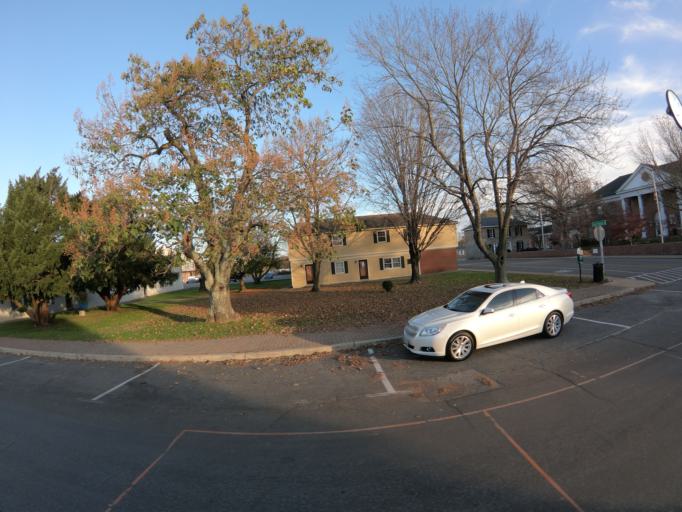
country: US
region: Maryland
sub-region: Saint Mary's County
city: Leonardtown
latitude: 38.2898
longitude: -76.6362
